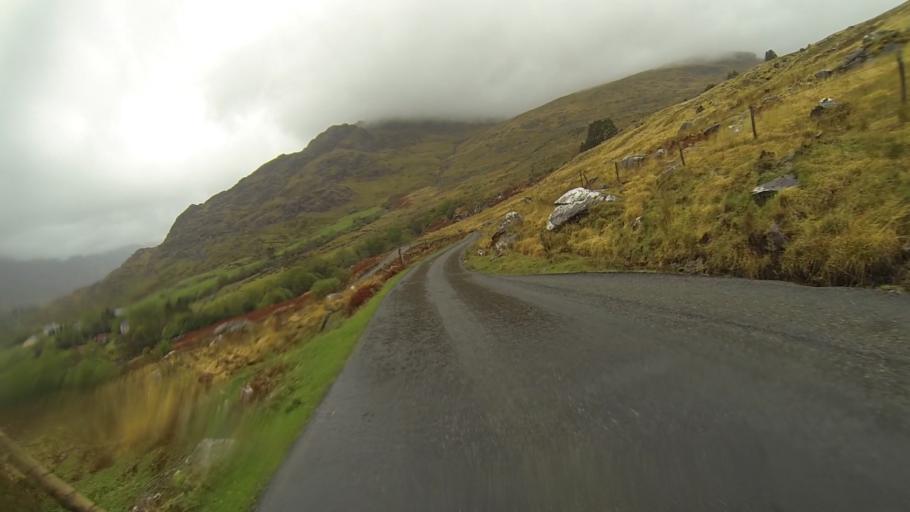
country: IE
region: Munster
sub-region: Ciarrai
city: Kenmare
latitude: 51.9892
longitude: -9.6608
